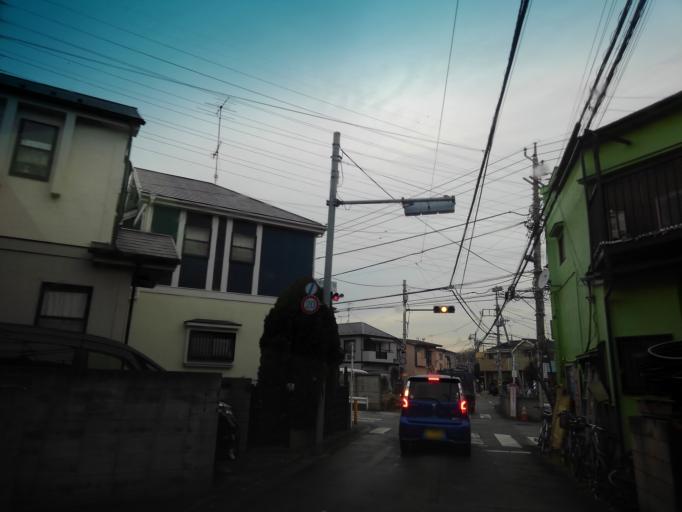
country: JP
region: Tokyo
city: Kokubunji
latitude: 35.7137
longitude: 139.4440
